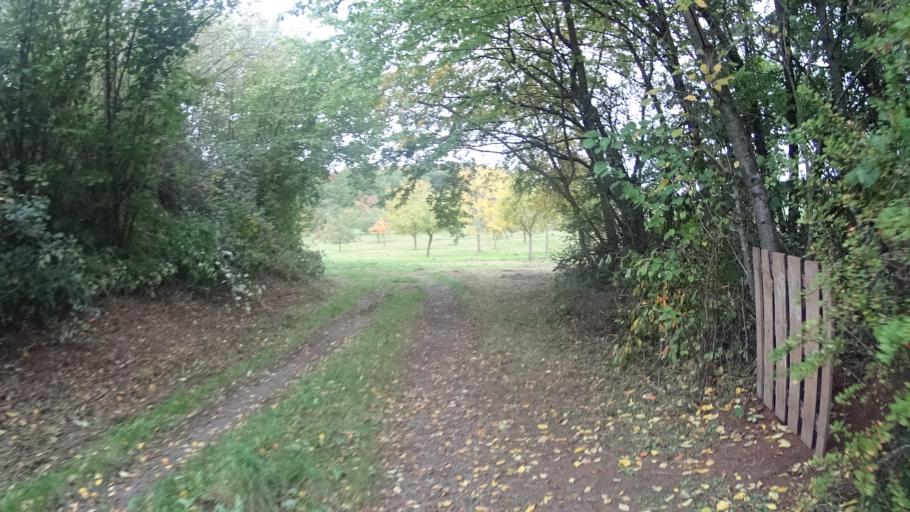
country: DE
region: Rheinland-Pfalz
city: Bolanden
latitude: 49.6376
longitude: 8.0013
